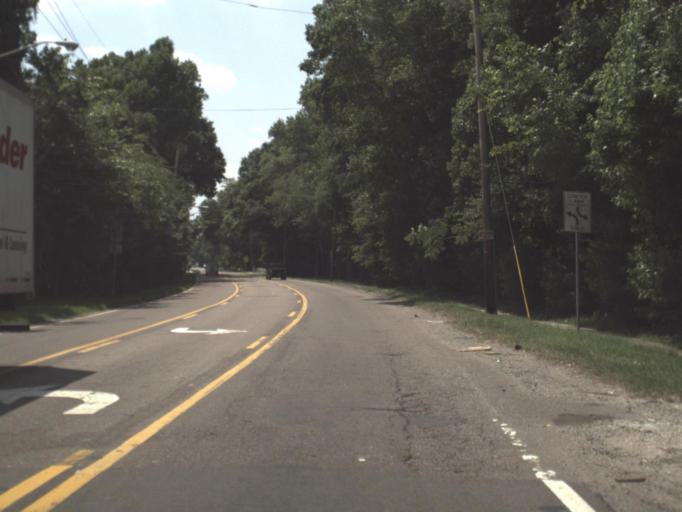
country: US
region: Florida
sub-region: Duval County
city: Jacksonville
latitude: 30.3741
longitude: -81.7485
